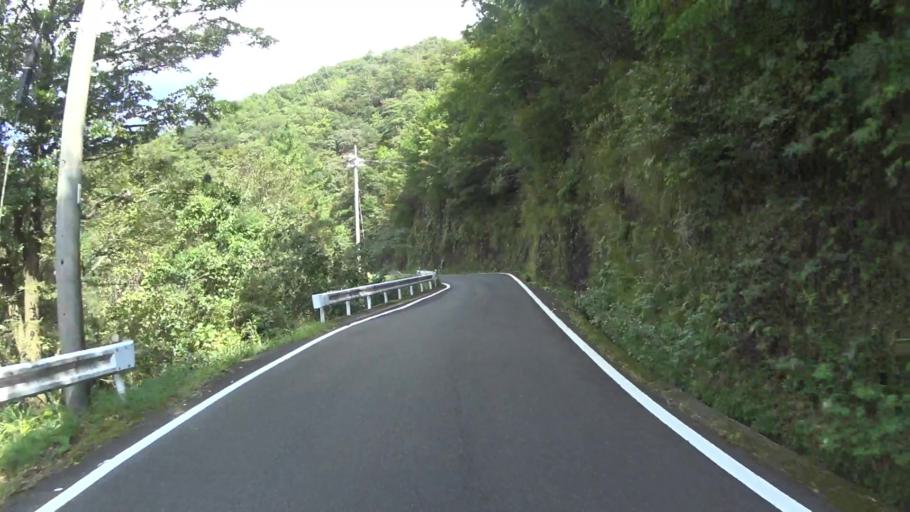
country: JP
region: Kyoto
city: Miyazu
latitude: 35.6778
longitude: 135.2663
